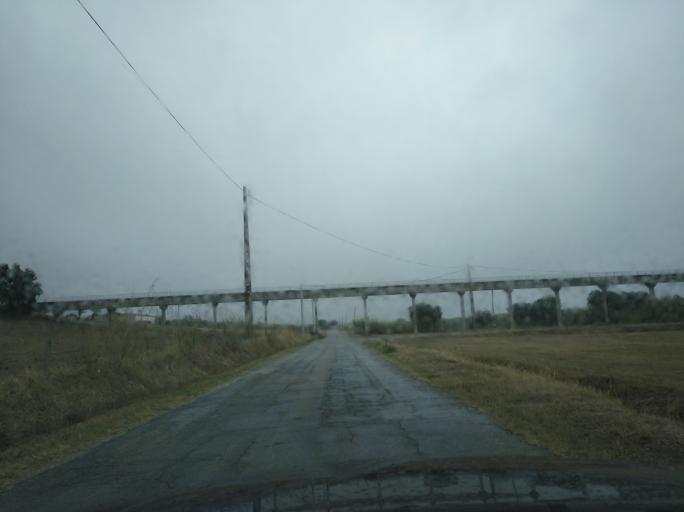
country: PT
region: Portalegre
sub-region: Campo Maior
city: Campo Maior
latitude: 38.9736
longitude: -7.0694
